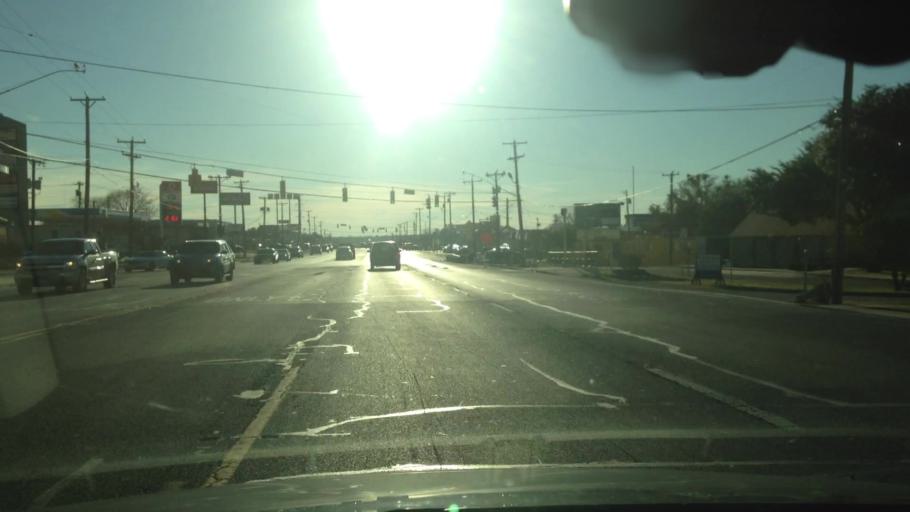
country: US
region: Texas
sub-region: Bexar County
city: Windcrest
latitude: 29.5108
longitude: -98.4072
